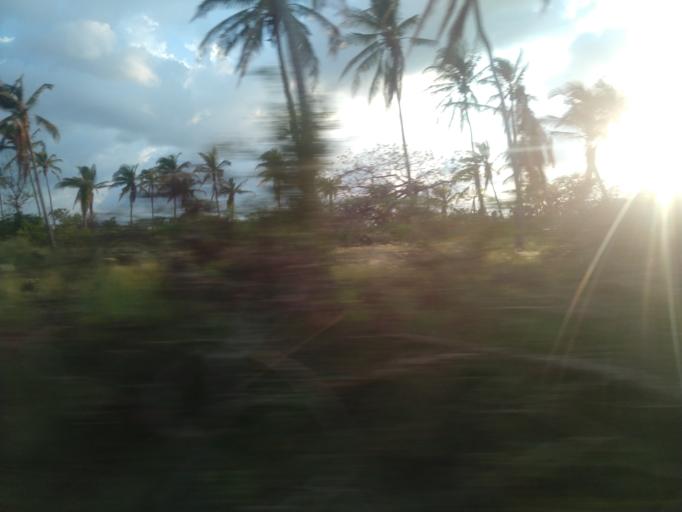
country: MZ
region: Sofala
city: Beira
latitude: -19.6734
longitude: 35.1263
